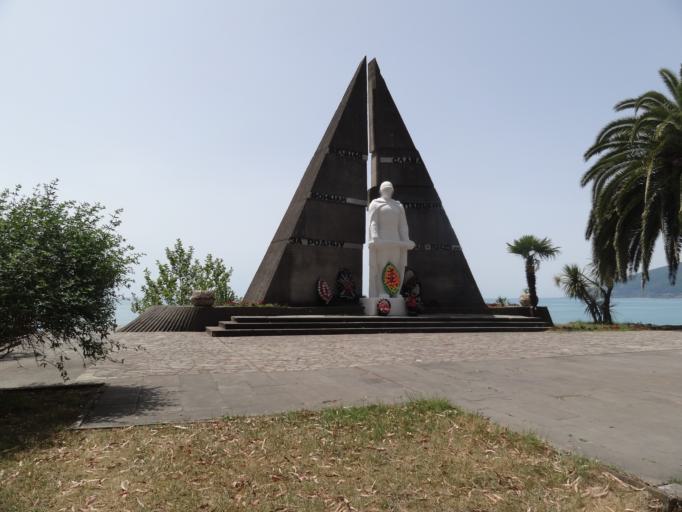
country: GE
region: Abkhazia
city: Gagra
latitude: 43.3014
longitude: 40.2560
